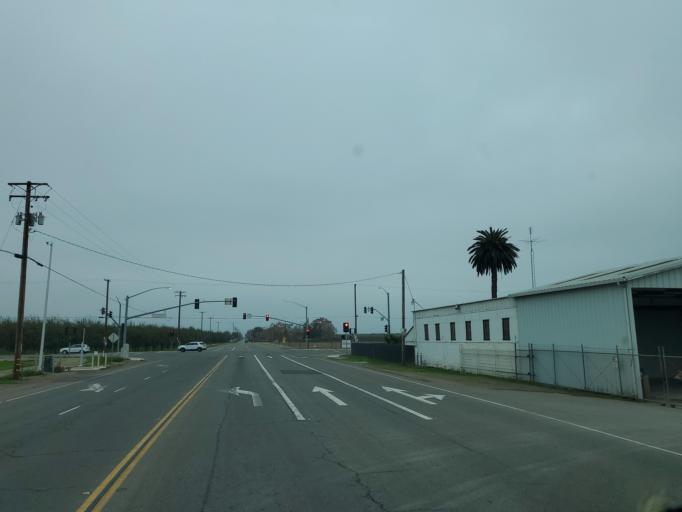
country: US
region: California
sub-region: Stanislaus County
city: Hughson
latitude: 37.5511
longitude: -120.8482
